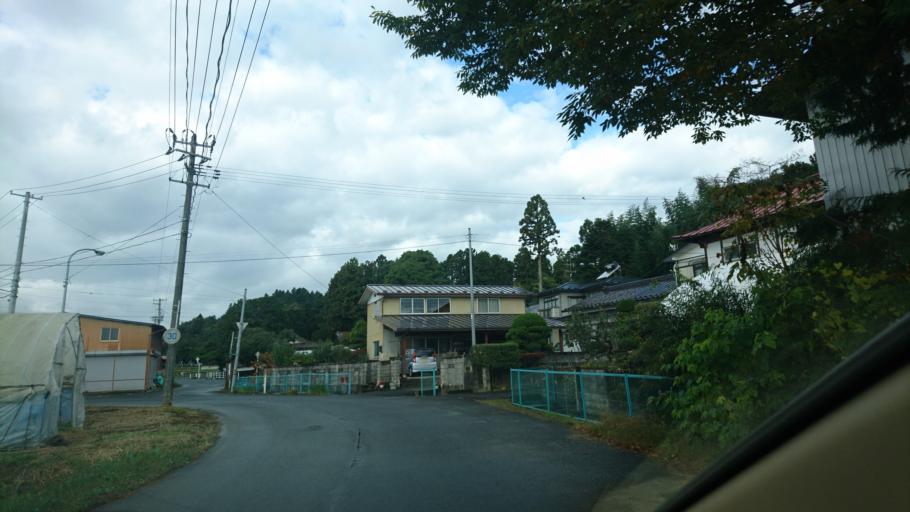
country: JP
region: Iwate
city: Ichinoseki
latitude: 38.7812
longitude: 141.0102
